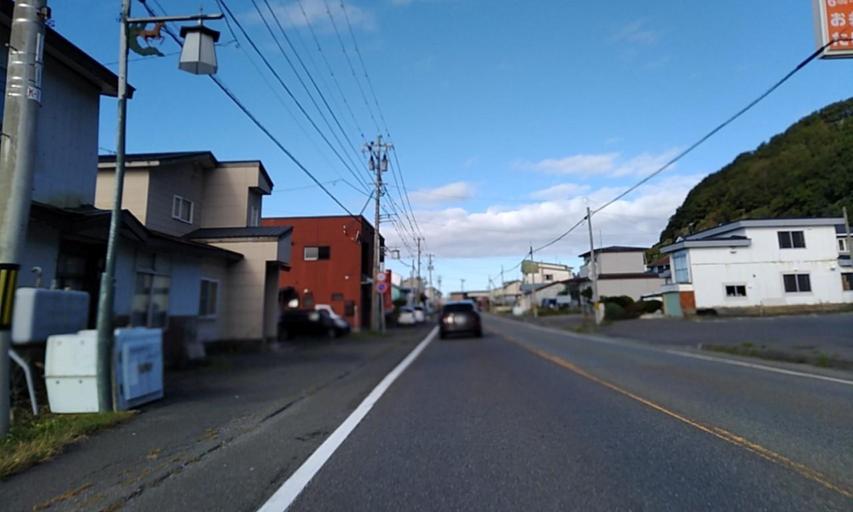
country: JP
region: Hokkaido
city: Shizunai-furukawacho
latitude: 42.2511
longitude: 142.5466
